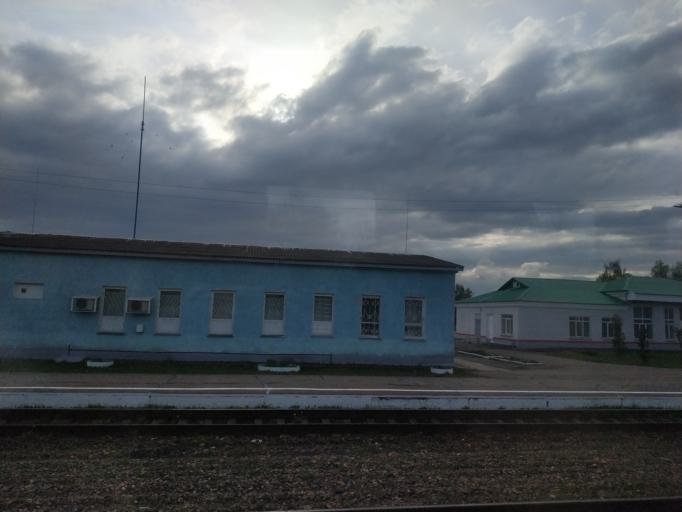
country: RU
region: Smolensk
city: Ugra
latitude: 54.7779
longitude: 34.3423
